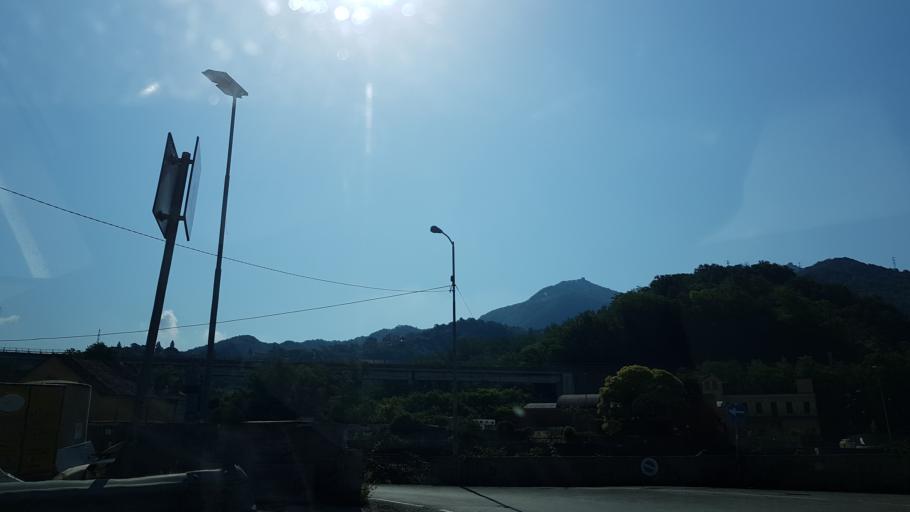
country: IT
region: Liguria
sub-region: Provincia di Genova
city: Manesseno
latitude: 44.4717
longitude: 8.9083
